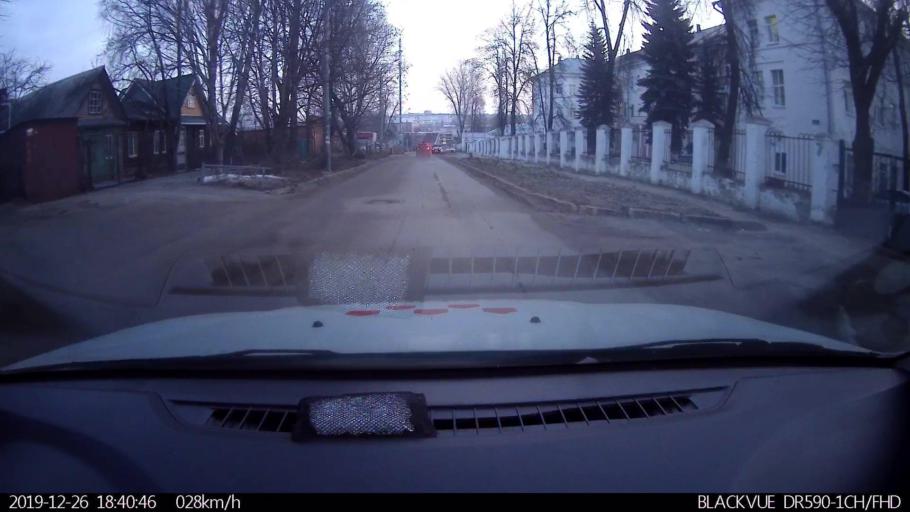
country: RU
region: Nizjnij Novgorod
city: Nizhniy Novgorod
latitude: 56.3139
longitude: 44.0325
